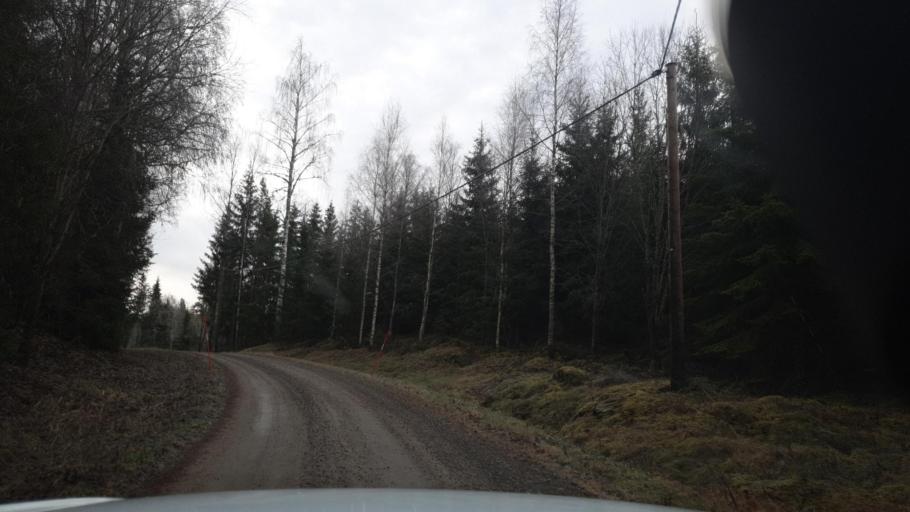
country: SE
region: Vaermland
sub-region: Karlstads Kommun
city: Edsvalla
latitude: 59.6087
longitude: 12.9872
